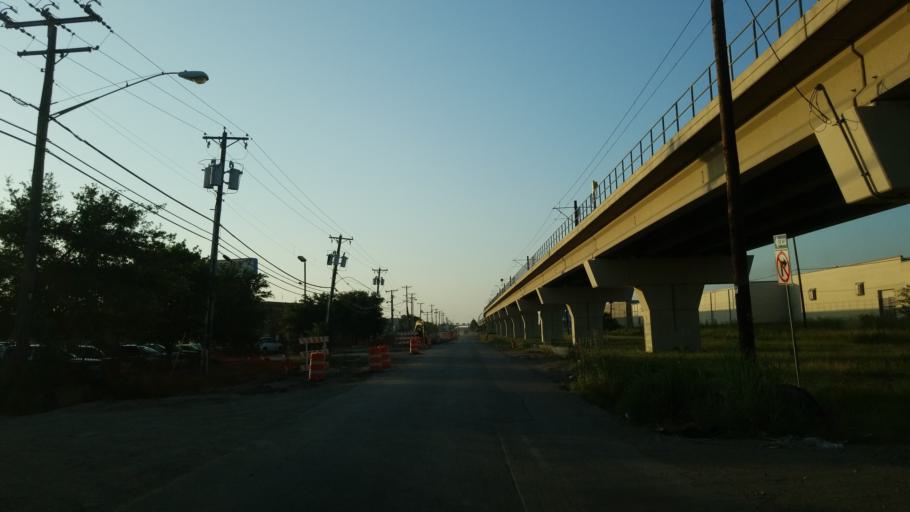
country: US
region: Texas
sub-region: Dallas County
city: Farmers Branch
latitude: 32.8912
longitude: -96.8869
